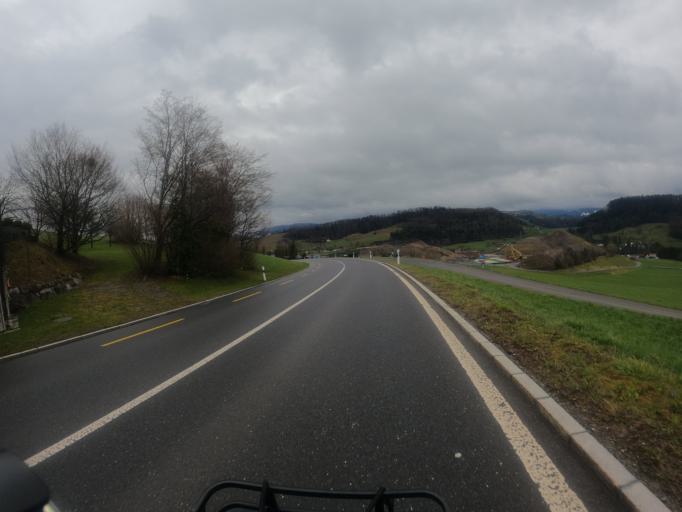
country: CH
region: Zurich
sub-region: Bezirk Affoltern
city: Hausen am Albis / Hausen (Dorf)
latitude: 47.2196
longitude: 8.5594
